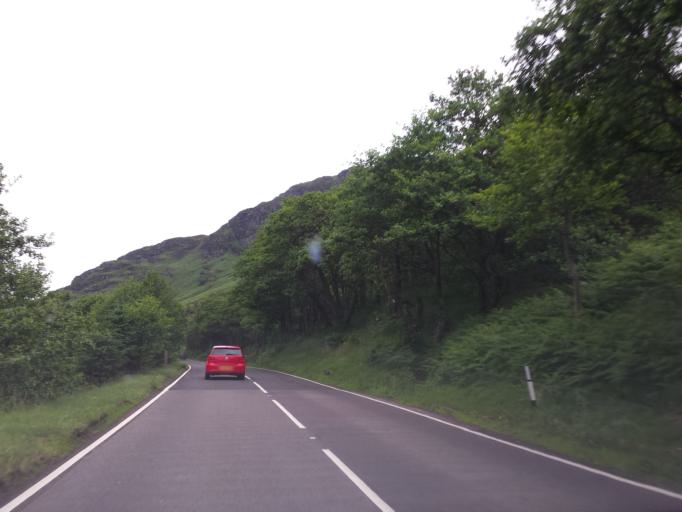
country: GB
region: Scotland
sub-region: Stirling
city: Callander
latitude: 56.4051
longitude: -4.3052
